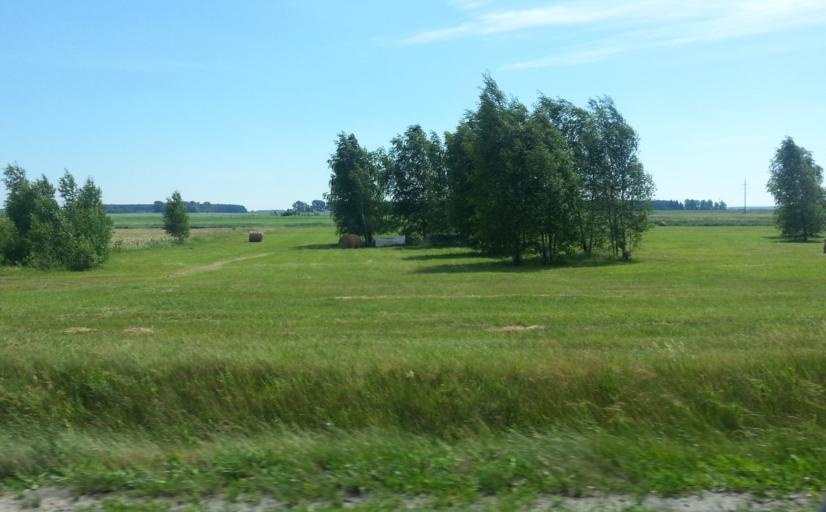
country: LT
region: Panevezys
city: Pasvalys
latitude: 55.9215
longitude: 24.3348
